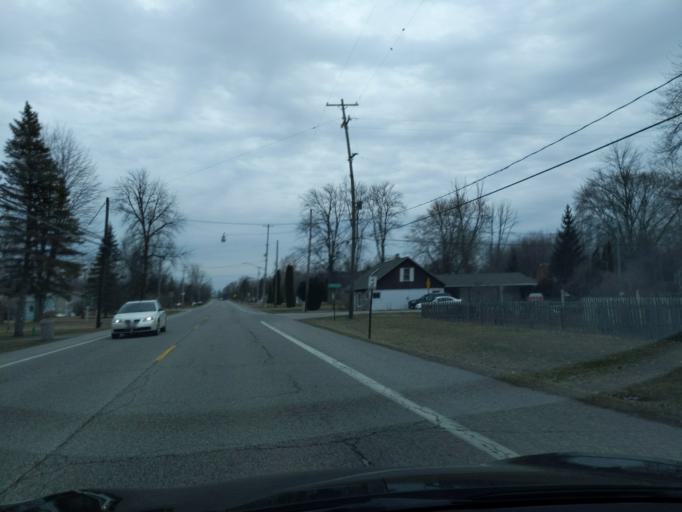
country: US
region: Michigan
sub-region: Bay County
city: Bay City
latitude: 43.6470
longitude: -83.9131
